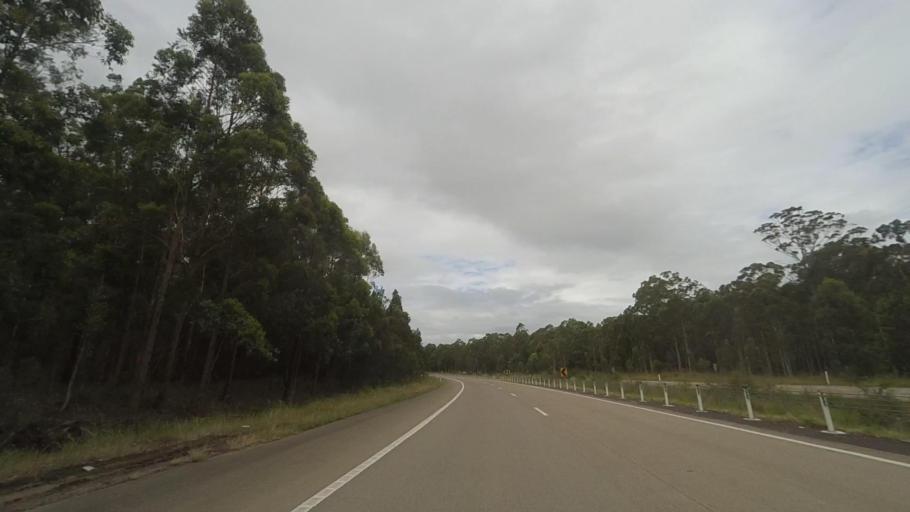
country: AU
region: New South Wales
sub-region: Port Stephens Shire
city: Medowie
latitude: -32.6509
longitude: 151.9064
